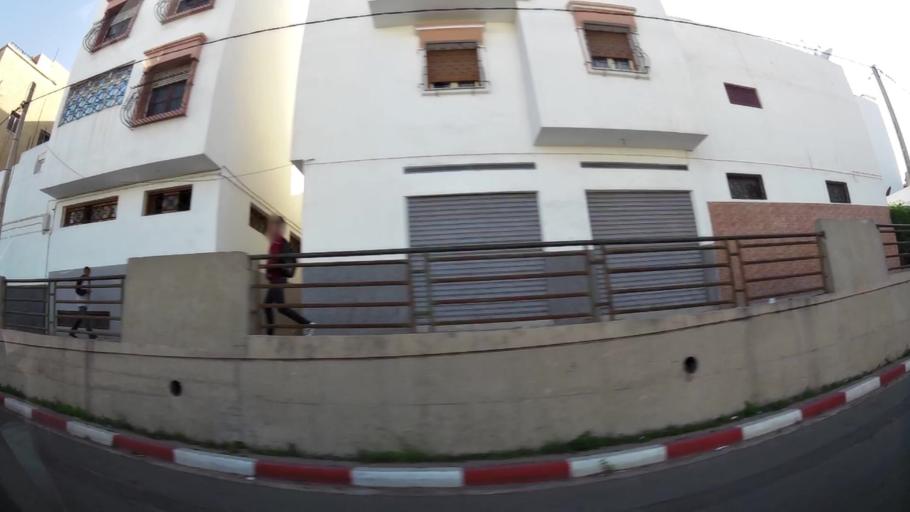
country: MA
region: Souss-Massa-Draa
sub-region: Agadir-Ida-ou-Tnan
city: Agadir
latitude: 30.4164
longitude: -9.5921
